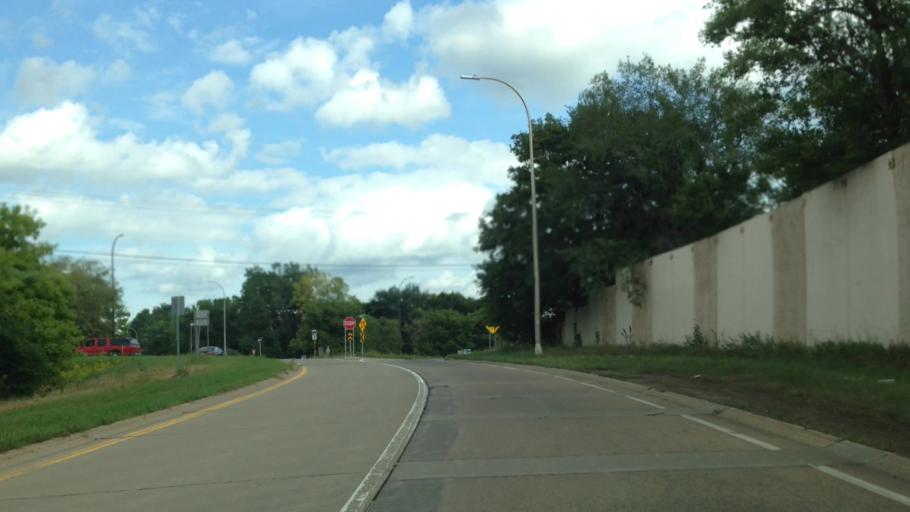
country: US
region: Minnesota
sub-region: Ramsey County
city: New Brighton
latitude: 45.0648
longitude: -93.2028
